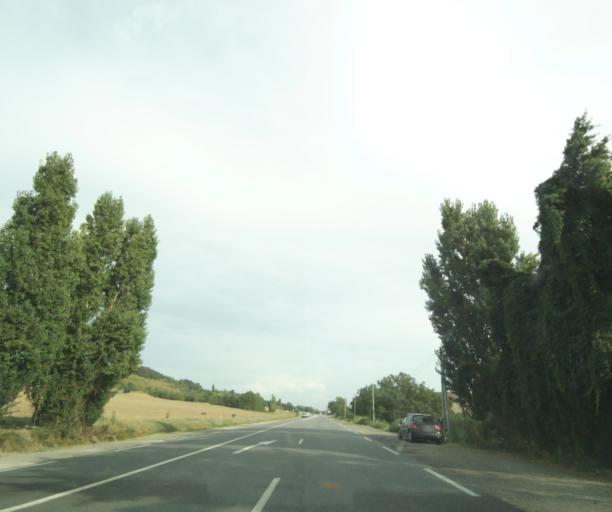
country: FR
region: Midi-Pyrenees
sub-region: Departement du Tarn-et-Garonne
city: Pompignan
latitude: 43.8027
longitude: 1.3272
